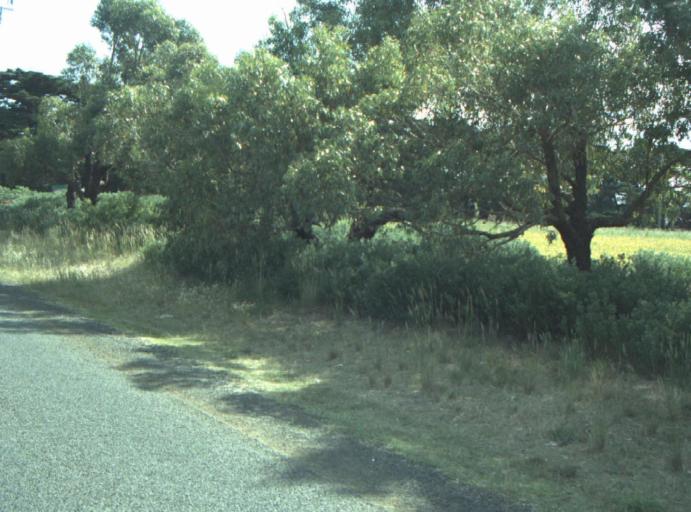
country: AU
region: Victoria
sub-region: Greater Geelong
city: Leopold
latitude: -38.1852
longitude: 144.5121
